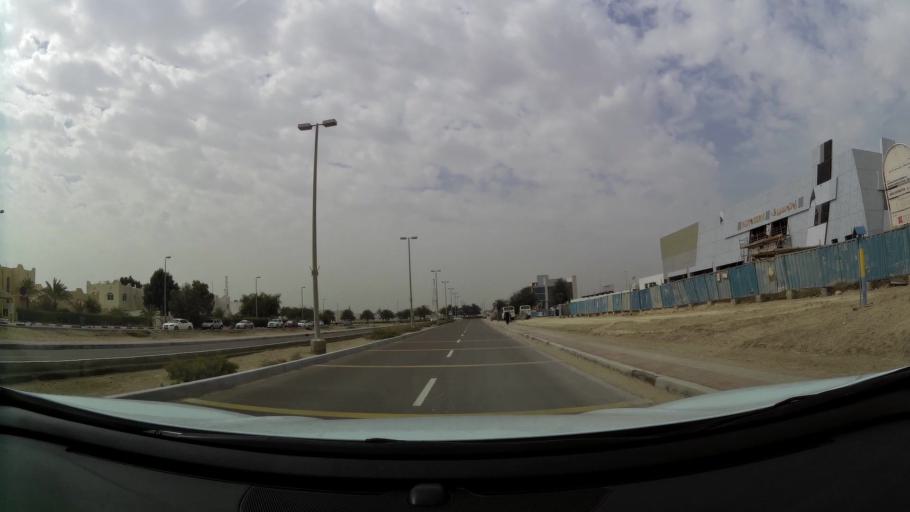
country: AE
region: Abu Dhabi
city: Abu Dhabi
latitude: 24.3199
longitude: 54.6144
